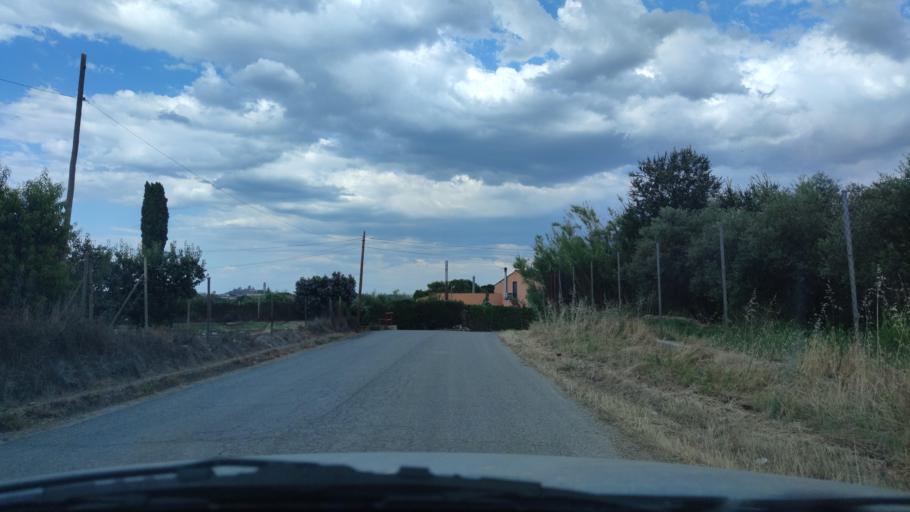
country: ES
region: Catalonia
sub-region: Provincia de Lleida
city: Lleida
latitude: 41.6115
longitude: 0.5822
